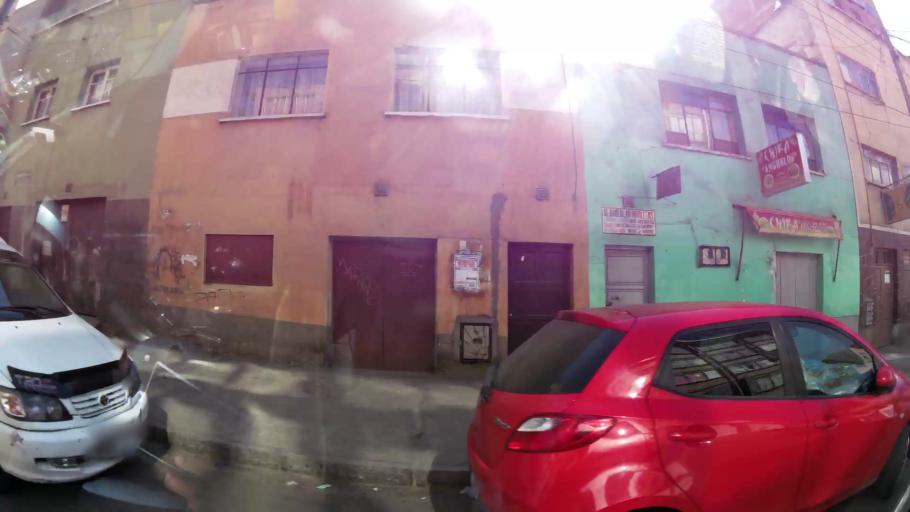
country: BO
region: La Paz
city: La Paz
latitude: -16.5083
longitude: -68.1433
